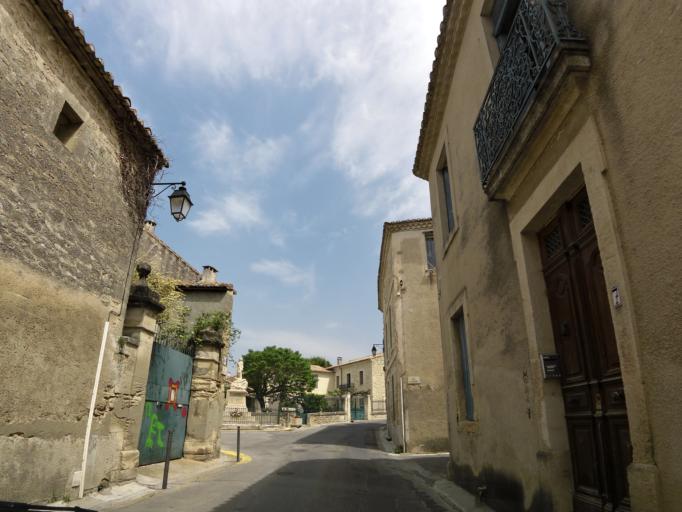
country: FR
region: Languedoc-Roussillon
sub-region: Departement du Gard
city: Aubais
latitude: 43.7698
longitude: 4.1230
